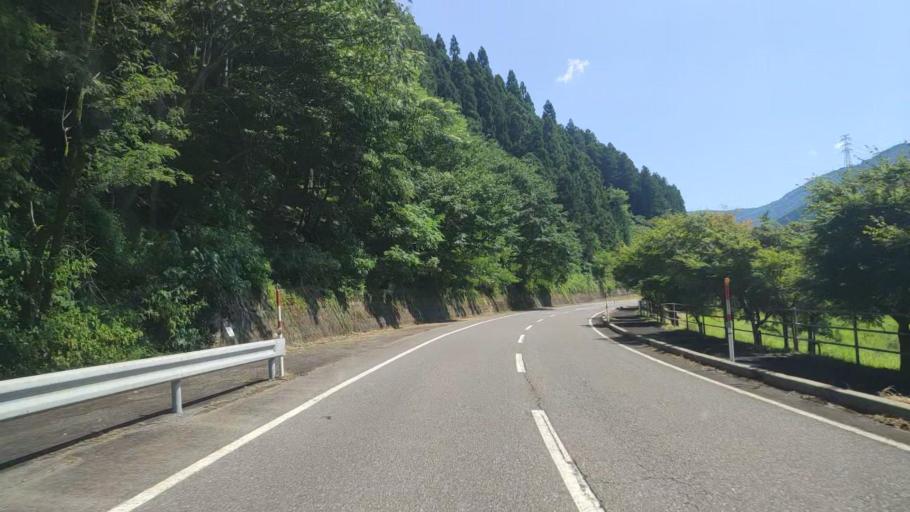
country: JP
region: Gifu
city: Godo
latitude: 35.6007
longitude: 136.6293
